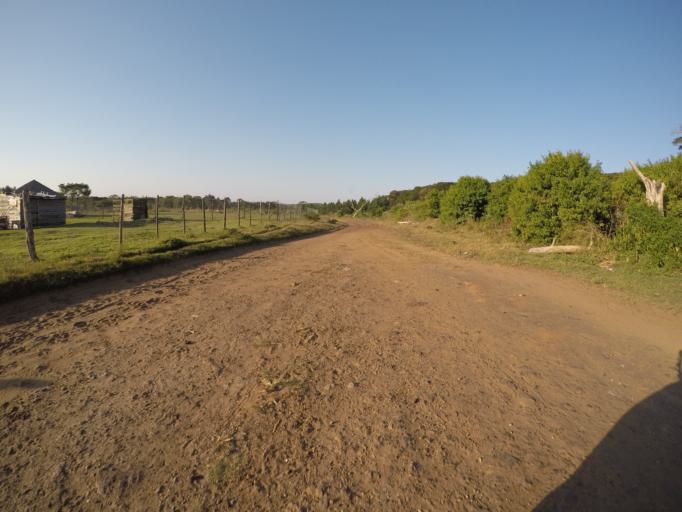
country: ZA
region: KwaZulu-Natal
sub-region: uThungulu District Municipality
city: KwaMbonambi
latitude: -28.6931
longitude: 32.1998
